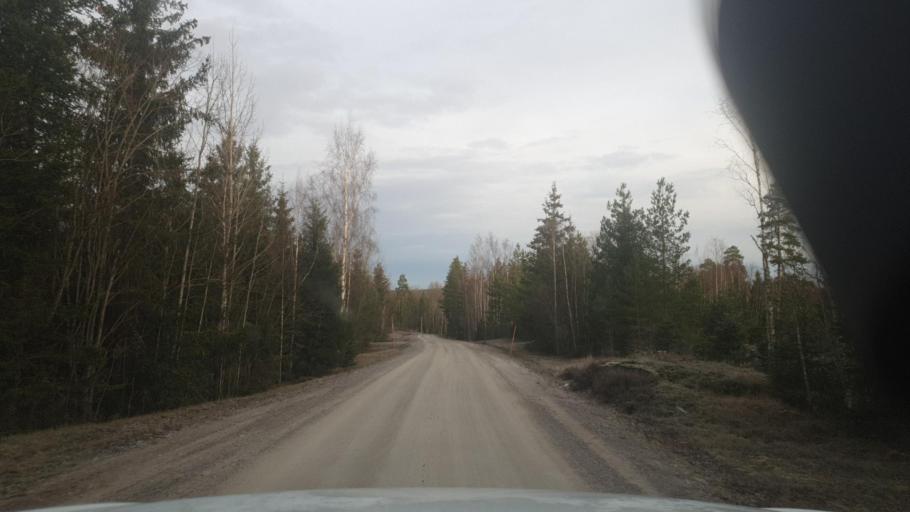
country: SE
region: Vaermland
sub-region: Arvika Kommun
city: Arvika
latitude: 59.5233
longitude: 12.7346
